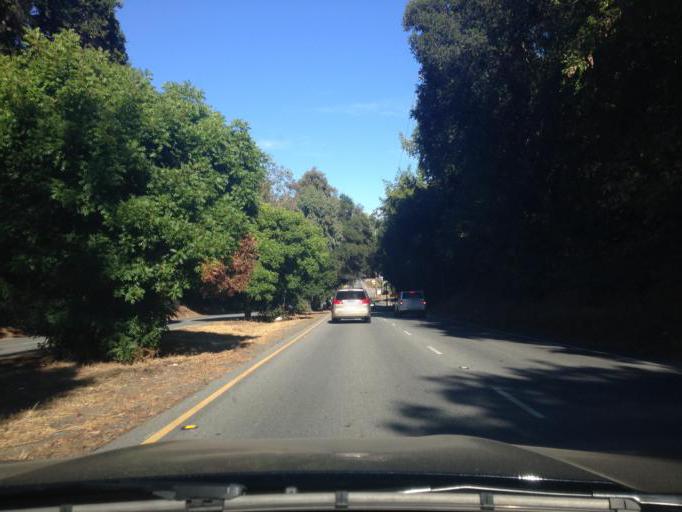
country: US
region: California
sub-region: Santa Clara County
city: Monte Sereno
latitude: 37.2419
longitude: -122.0043
